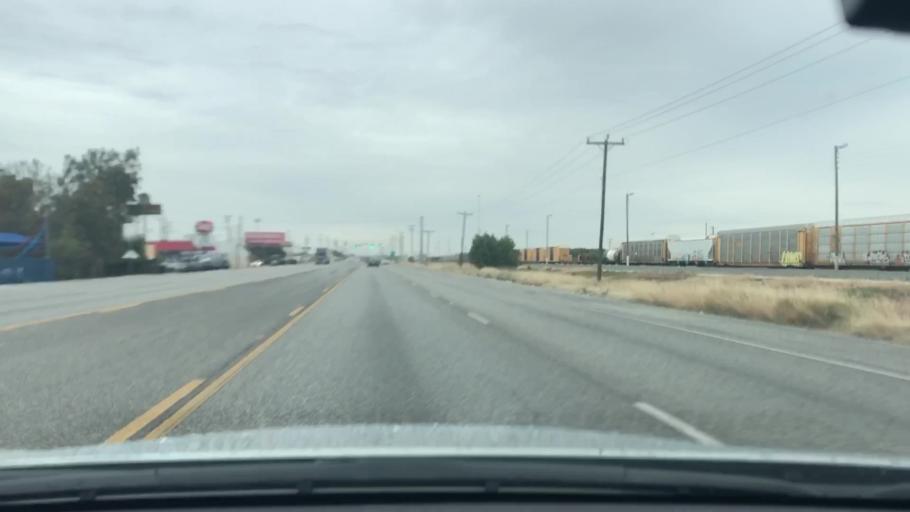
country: US
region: Texas
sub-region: Bexar County
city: Kirby
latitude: 29.4657
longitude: -98.3953
